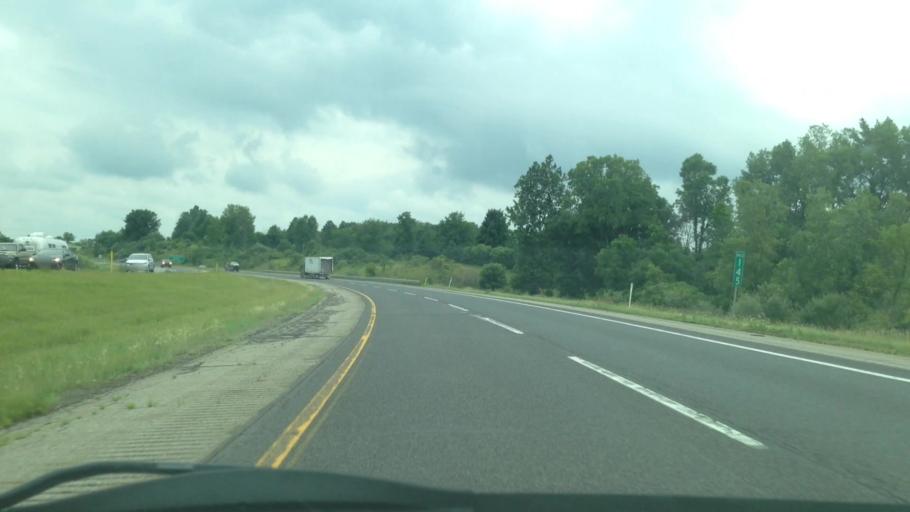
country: US
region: Indiana
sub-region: Steuben County
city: Fremont
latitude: 41.7342
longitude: -84.9749
